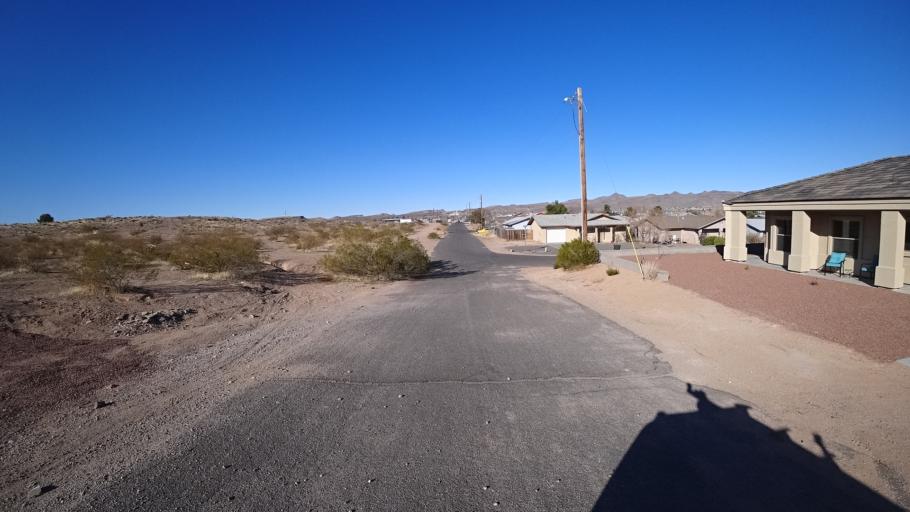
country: US
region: Arizona
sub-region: Mohave County
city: Kingman
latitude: 35.2104
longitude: -114.0090
